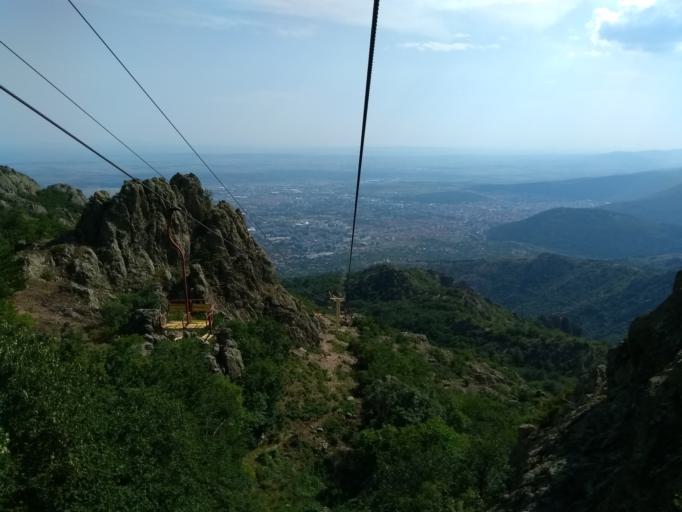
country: BG
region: Sliven
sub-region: Obshtina Sliven
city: Sliven
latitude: 42.7177
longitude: 26.3589
